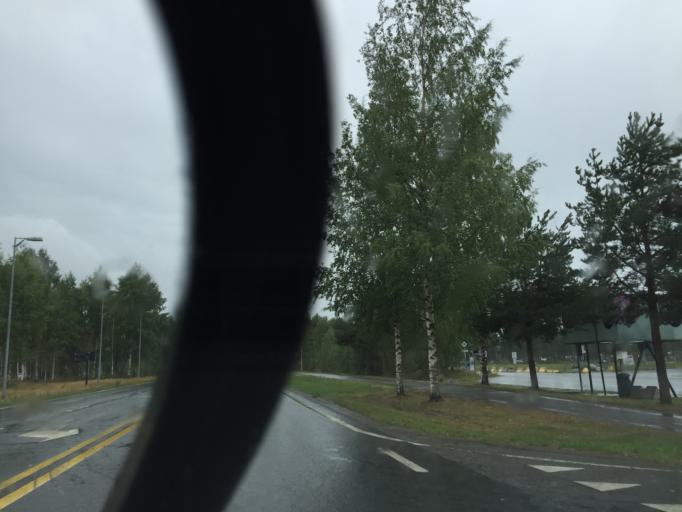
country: NO
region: Akershus
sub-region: Nannestad
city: Teigebyen
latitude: 60.1817
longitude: 11.0857
